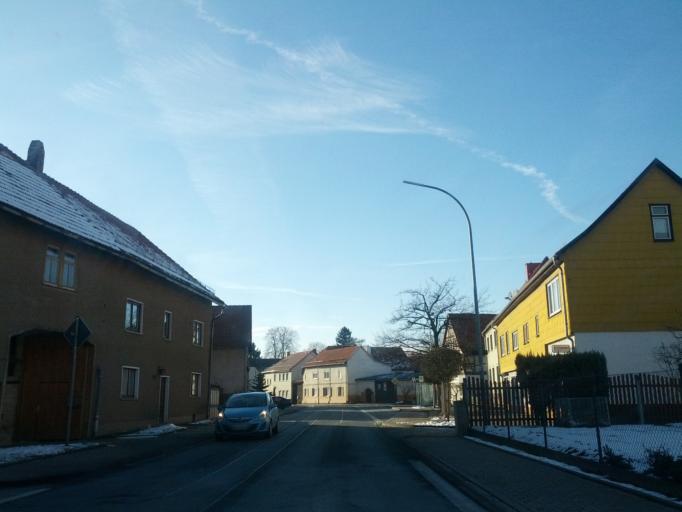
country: DE
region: Thuringia
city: Haina
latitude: 51.0216
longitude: 10.5115
